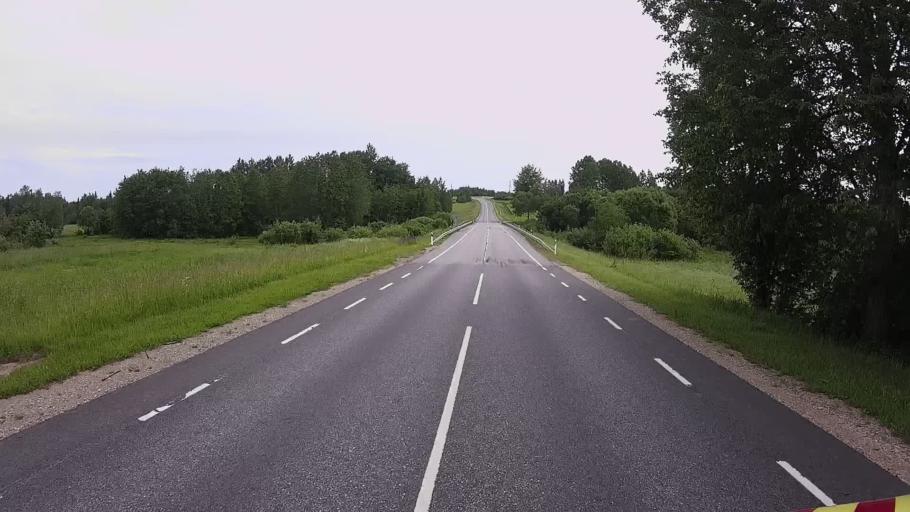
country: EE
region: Viljandimaa
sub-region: Karksi vald
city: Karksi-Nuia
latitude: 58.1462
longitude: 25.5917
